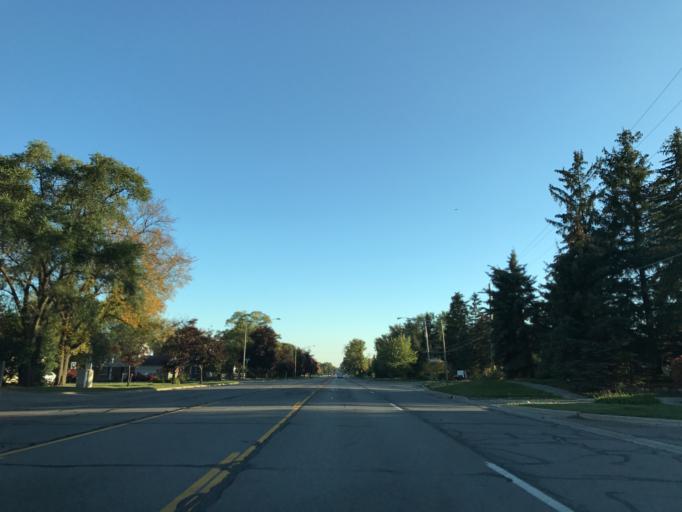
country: US
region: Michigan
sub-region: Oakland County
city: Farmington Hills
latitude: 42.4836
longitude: -83.3383
